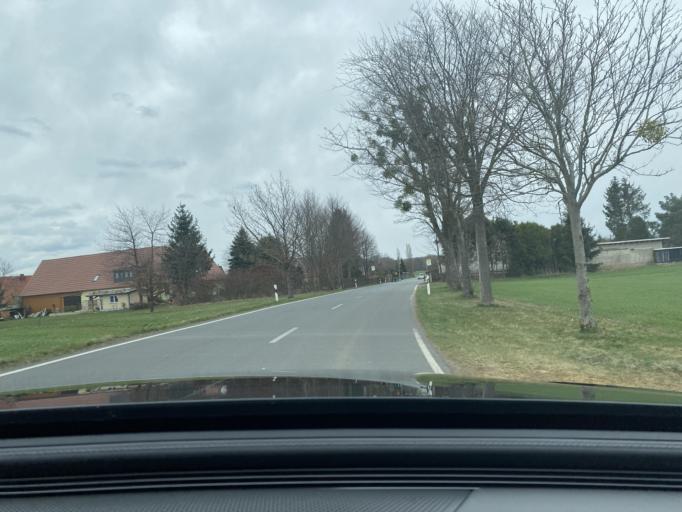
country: DE
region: Saxony
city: Durrrohrsdorf
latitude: 51.0262
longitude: 14.0299
